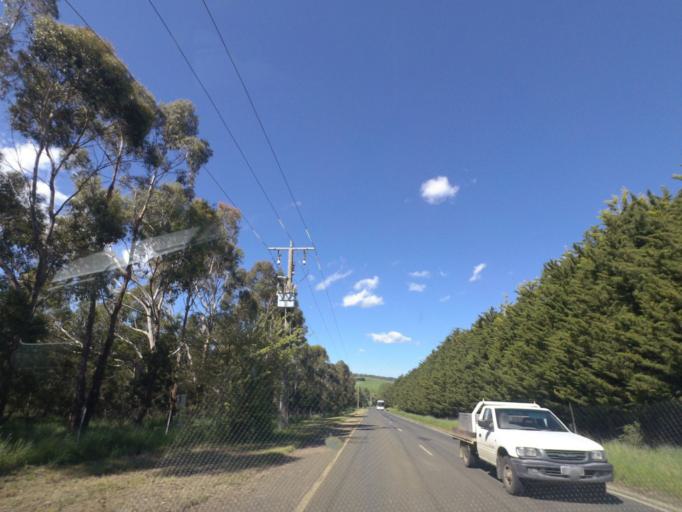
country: AU
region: Victoria
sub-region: Moorabool
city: Bacchus Marsh
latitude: -37.5646
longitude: 144.2620
